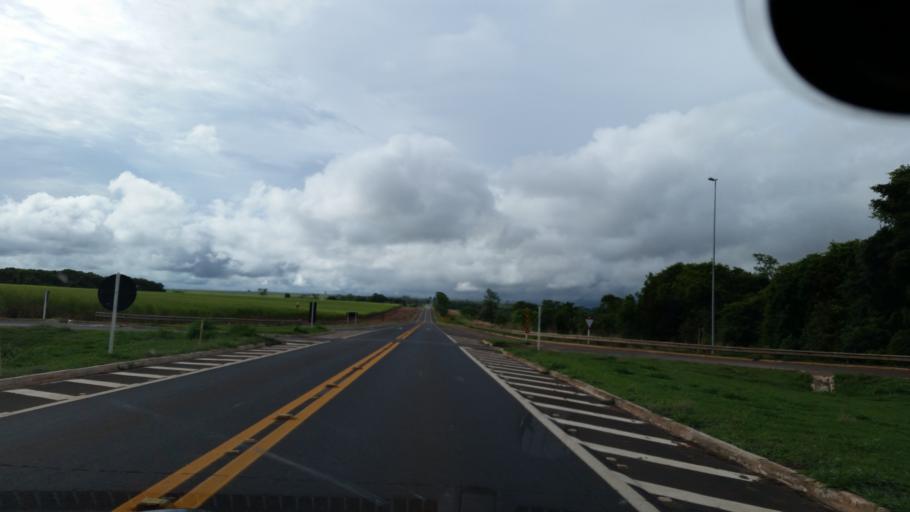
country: BR
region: Minas Gerais
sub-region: Tupaciguara
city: Tupaciguara
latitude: -18.7496
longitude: -48.6117
